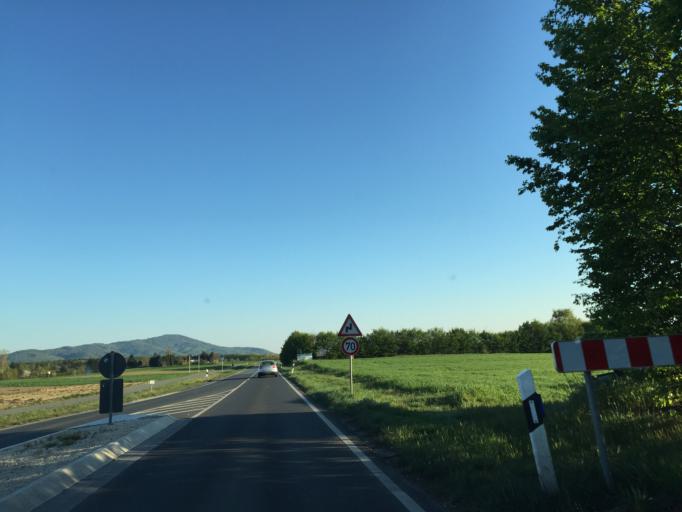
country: DE
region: Hesse
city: Pfungstadt
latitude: 49.7933
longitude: 8.6012
